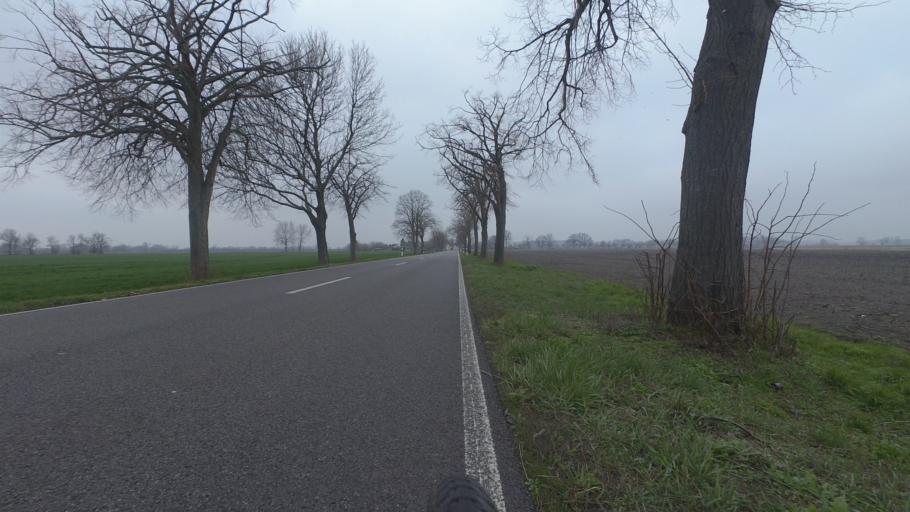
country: DE
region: Brandenburg
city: Nauen
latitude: 52.6279
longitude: 12.8567
